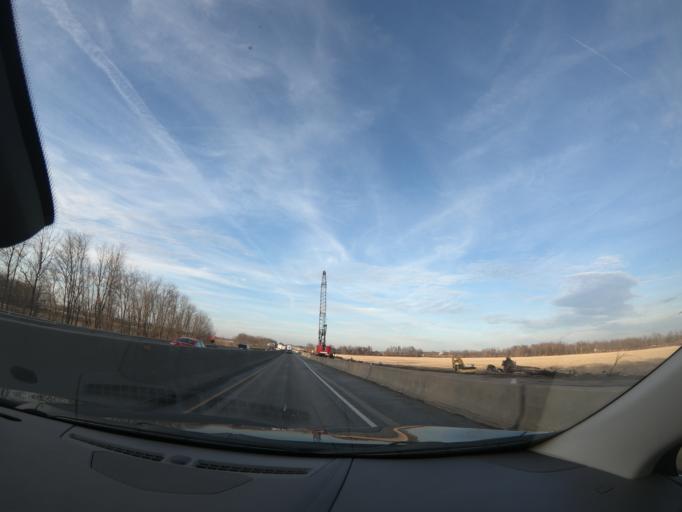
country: US
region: Kentucky
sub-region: Hardin County
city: Elizabethtown
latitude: 37.5607
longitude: -85.8762
